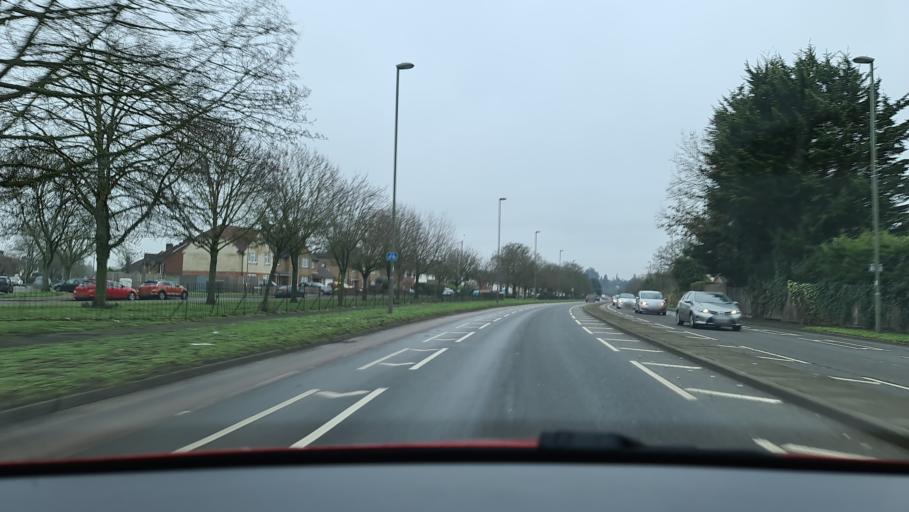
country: GB
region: England
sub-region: Surrey
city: Esher
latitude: 51.3686
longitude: -0.3930
